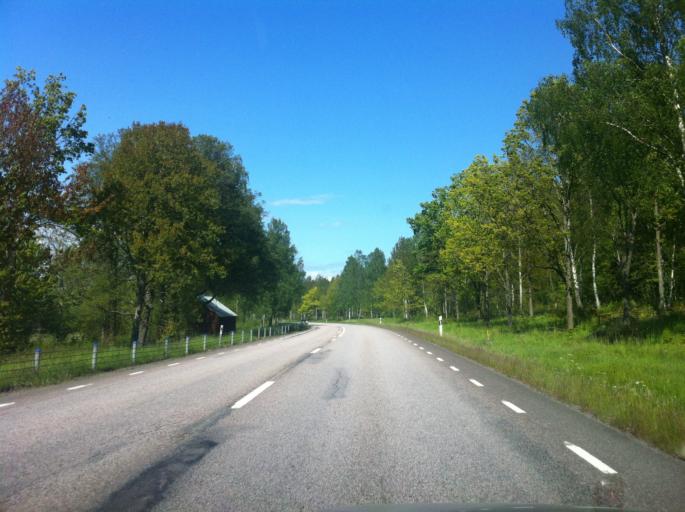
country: SE
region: Vaestra Goetaland
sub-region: Gullspangs Kommun
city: Gullspang
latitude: 59.0208
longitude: 14.1226
